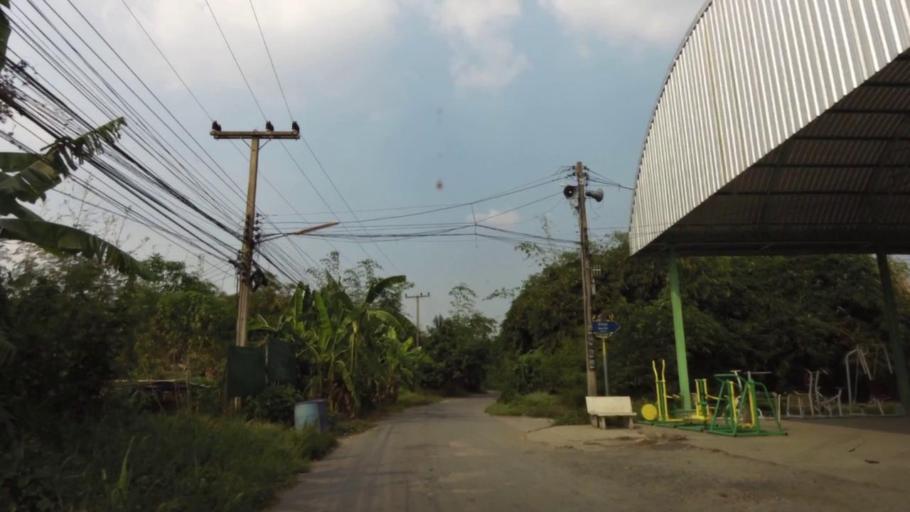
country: TH
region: Phra Nakhon Si Ayutthaya
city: Phra Nakhon Si Ayutthaya
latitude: 14.3082
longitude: 100.5648
